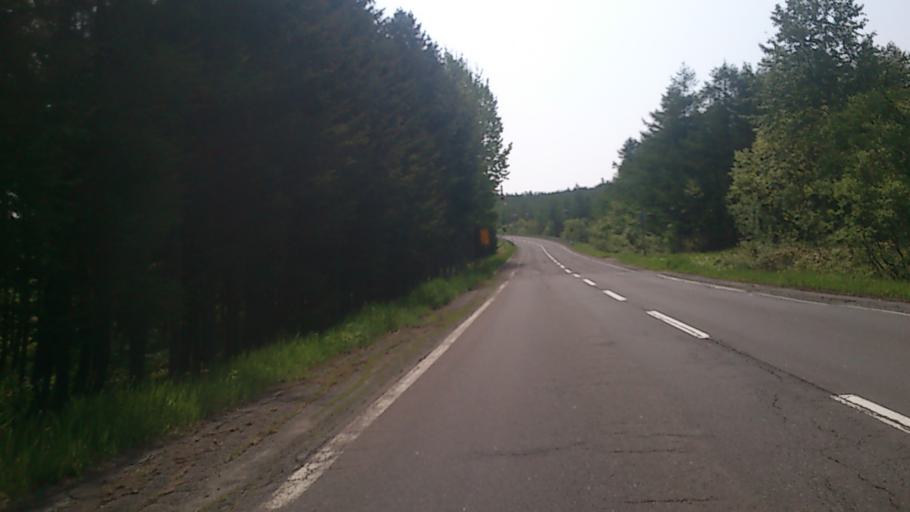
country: JP
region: Hokkaido
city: Kushiro
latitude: 43.4838
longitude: 144.5361
